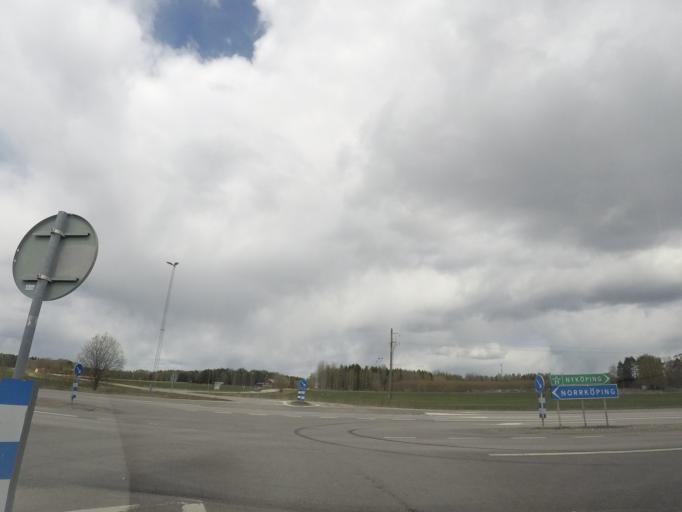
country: SE
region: Soedermanland
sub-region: Nykopings Kommun
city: Svalsta
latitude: 58.7429
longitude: 16.9162
